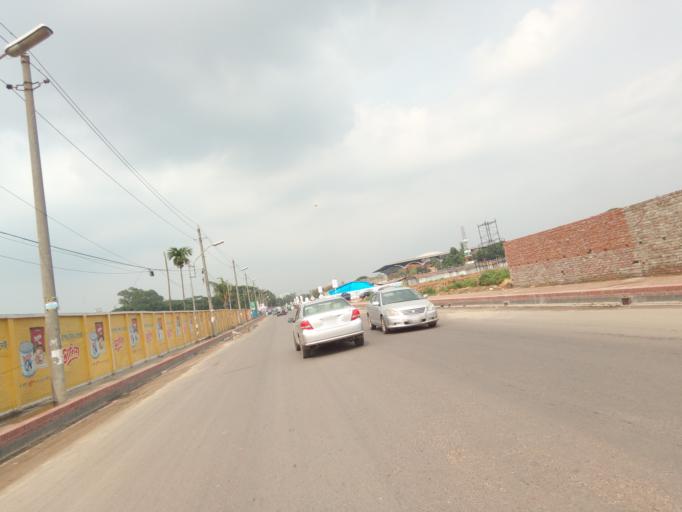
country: BD
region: Dhaka
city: Azimpur
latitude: 23.7700
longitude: 90.3765
